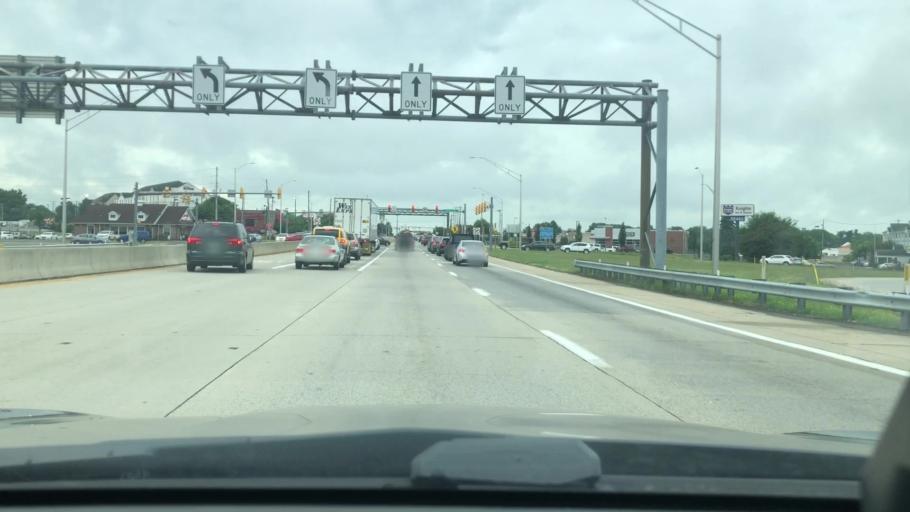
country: US
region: Pennsylvania
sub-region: Lehigh County
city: Fullerton
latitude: 40.6413
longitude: -75.4330
